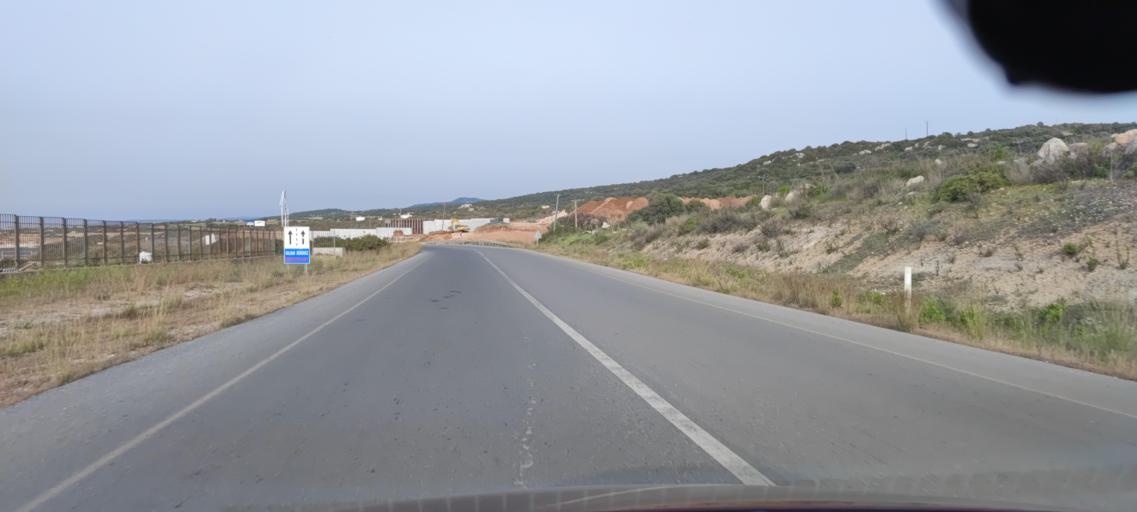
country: CY
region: Ammochostos
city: Leonarisso
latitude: 35.5565
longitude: 34.2312
